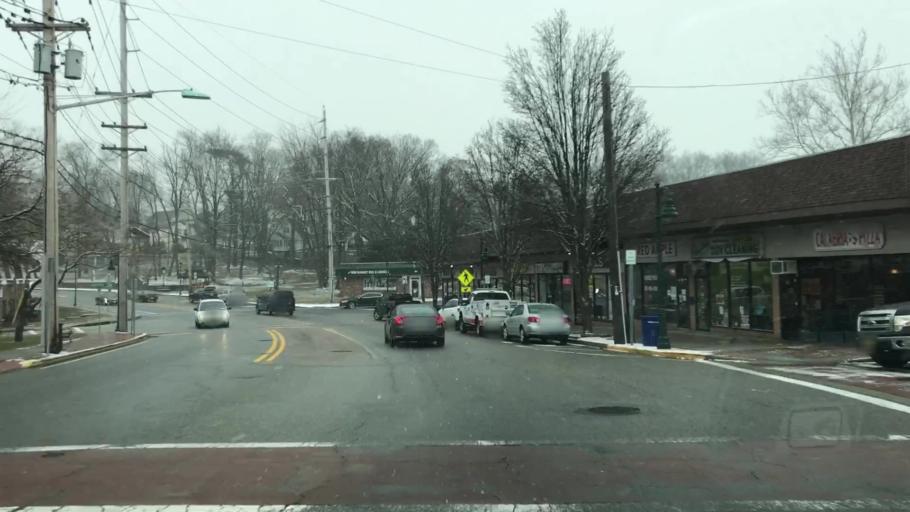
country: US
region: New Jersey
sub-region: Bergen County
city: Oradell
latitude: 40.9486
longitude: -74.0320
